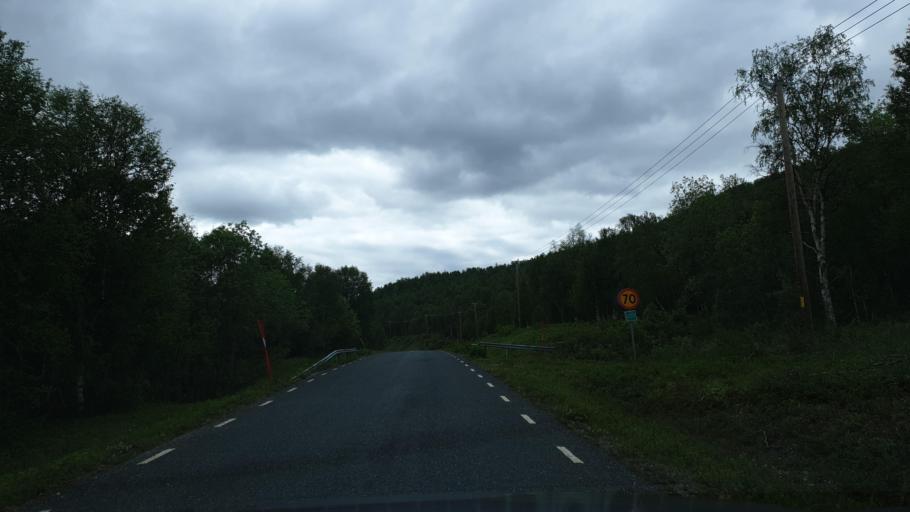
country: NO
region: Nordland
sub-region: Hattfjelldal
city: Hattfjelldal
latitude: 65.4184
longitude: 14.7692
